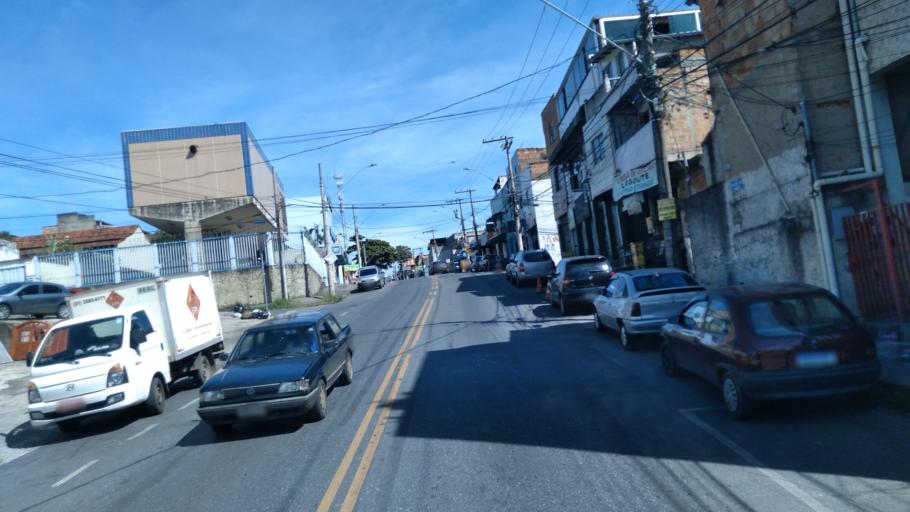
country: BR
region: Minas Gerais
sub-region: Contagem
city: Contagem
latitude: -19.8904
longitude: -44.0113
